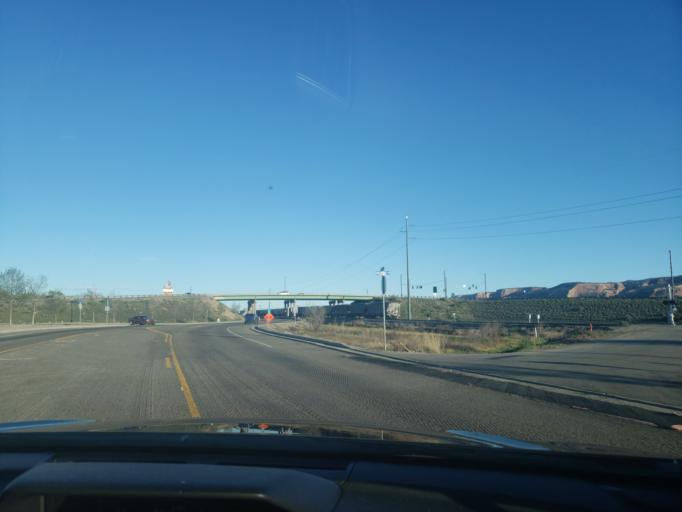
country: US
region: Colorado
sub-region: Mesa County
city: Fruita
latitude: 39.1581
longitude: -108.7384
